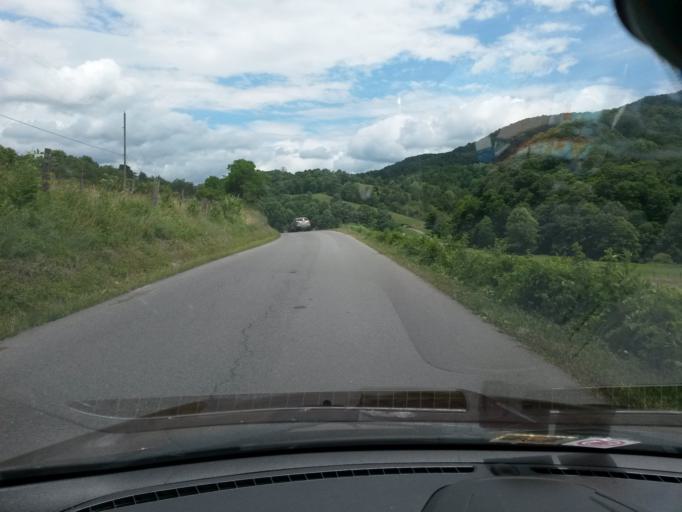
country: US
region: West Virginia
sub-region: Monroe County
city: Union
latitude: 37.5023
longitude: -80.5874
